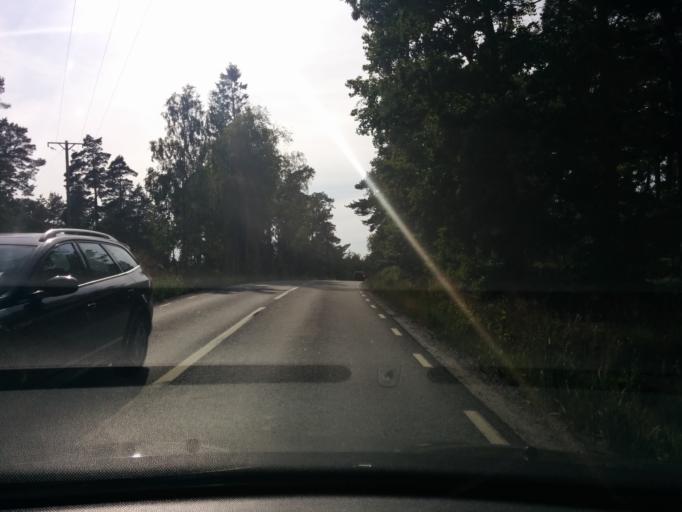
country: SE
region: Stockholm
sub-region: Varmdo Kommun
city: Holo
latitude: 59.2818
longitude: 18.6154
